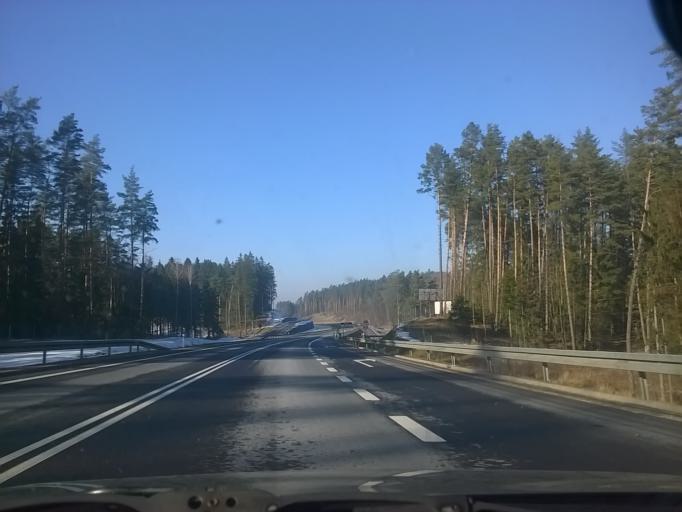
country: PL
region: Warmian-Masurian Voivodeship
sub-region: Powiat olsztynski
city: Barczewo
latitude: 53.8311
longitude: 20.7754
